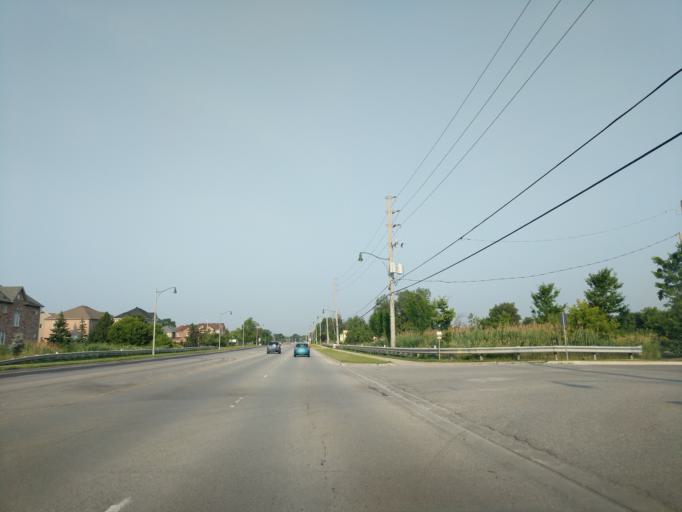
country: CA
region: Ontario
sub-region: York
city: Richmond Hill
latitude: 43.8962
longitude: -79.4062
